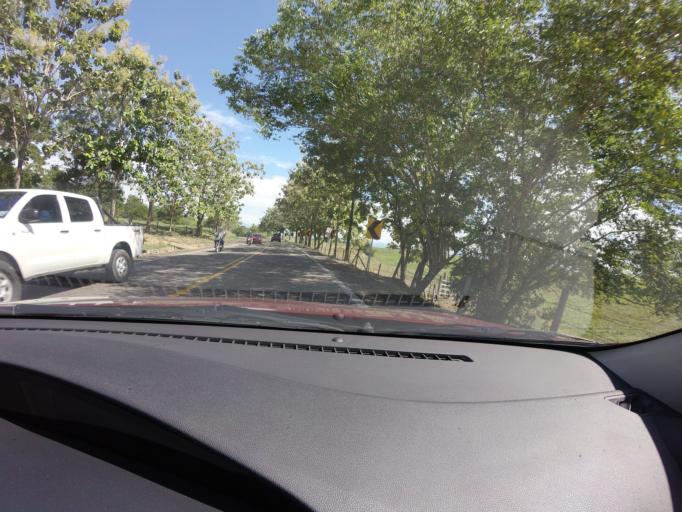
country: CO
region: Antioquia
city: Puerto Triunfo
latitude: 5.9003
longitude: -74.6333
